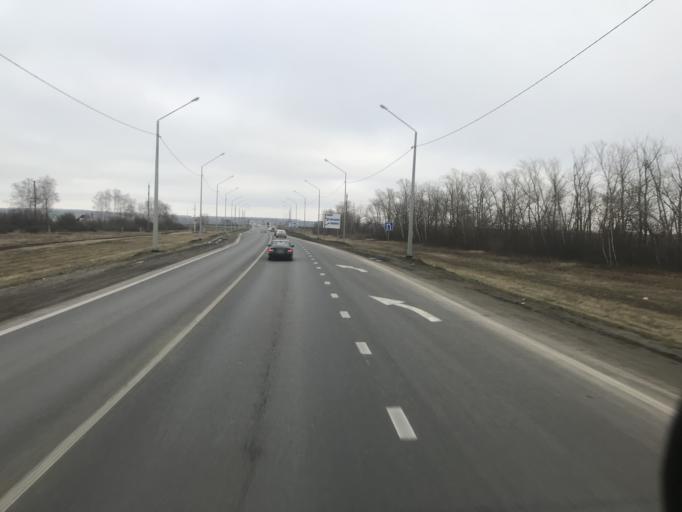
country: RU
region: Penza
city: Bogoslovka
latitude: 53.1309
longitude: 44.7690
